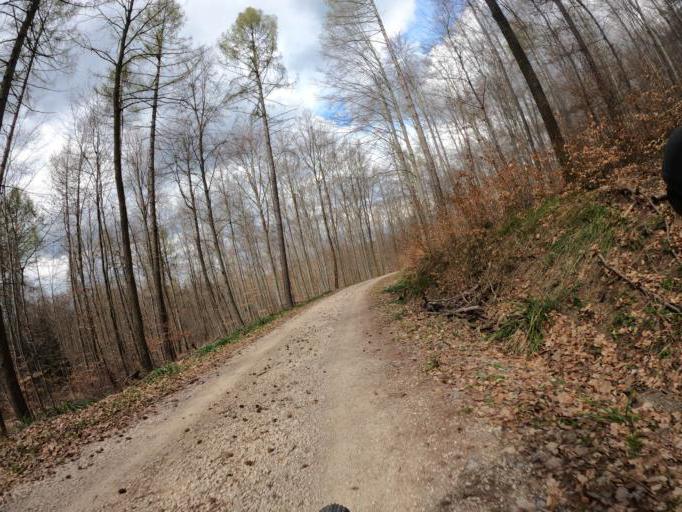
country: DE
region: Baden-Wuerttemberg
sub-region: Tuebingen Region
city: Gomaringen
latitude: 48.4295
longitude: 9.1156
